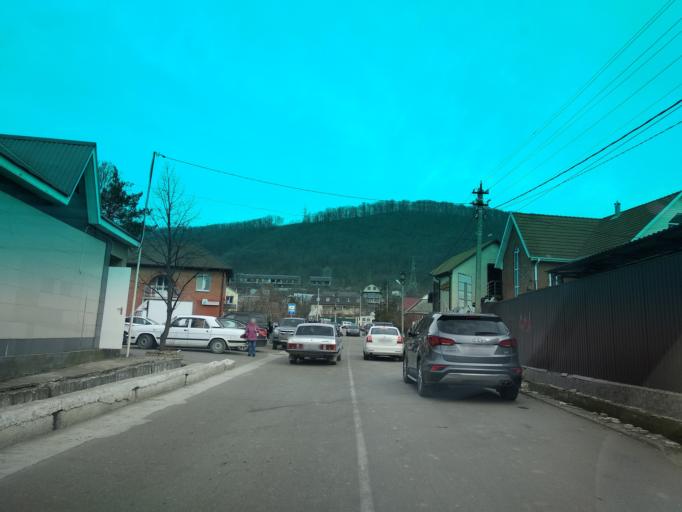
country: RU
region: Krasnodarskiy
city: Novomikhaylovskiy
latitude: 44.2500
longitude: 38.8389
